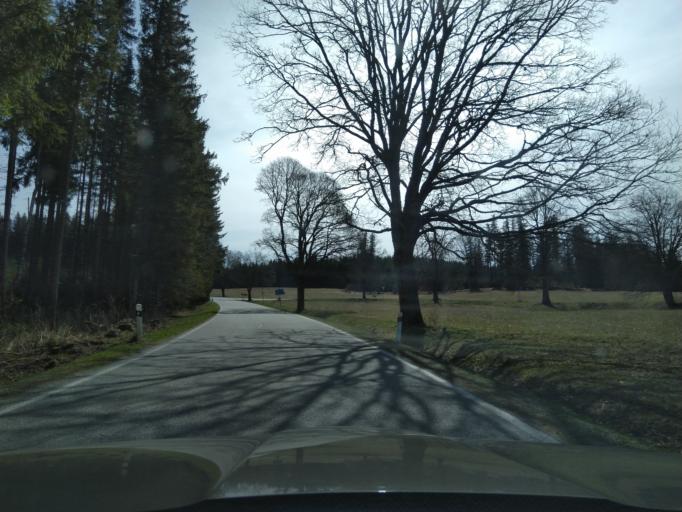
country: CZ
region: Jihocesky
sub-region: Okres Prachatice
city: Zdikov
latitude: 49.0455
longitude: 13.6724
